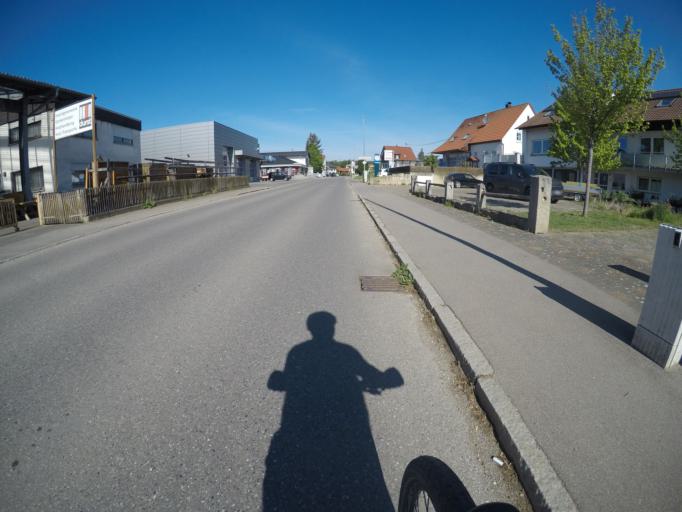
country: DE
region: Baden-Wuerttemberg
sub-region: Tuebingen Region
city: Pliezhausen
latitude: 48.5891
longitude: 9.1758
